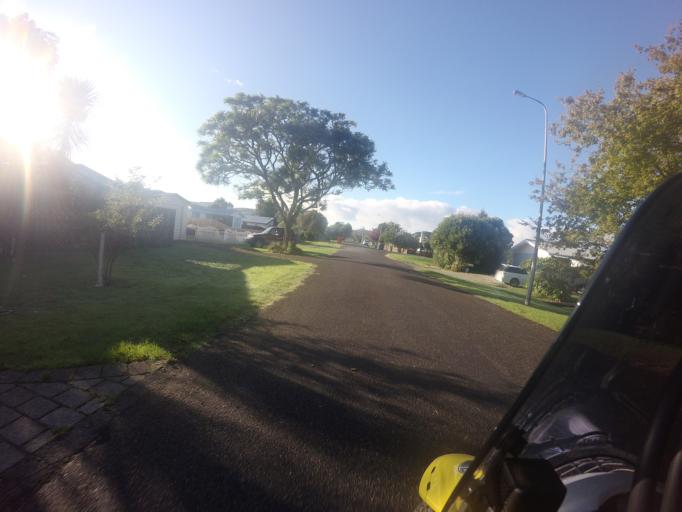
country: NZ
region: Gisborne
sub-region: Gisborne District
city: Gisborne
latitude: -38.6656
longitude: 178.0467
